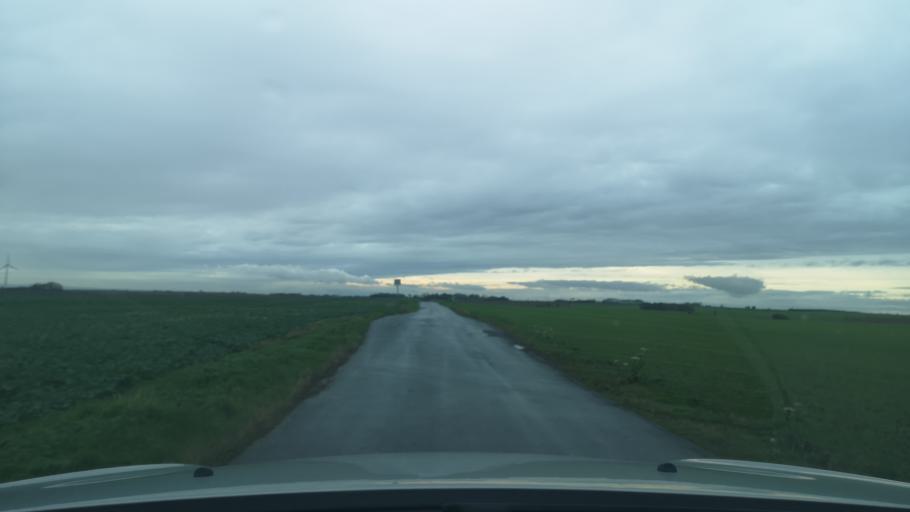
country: GB
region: England
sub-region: East Riding of Yorkshire
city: Holmpton
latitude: 53.6782
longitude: 0.0907
